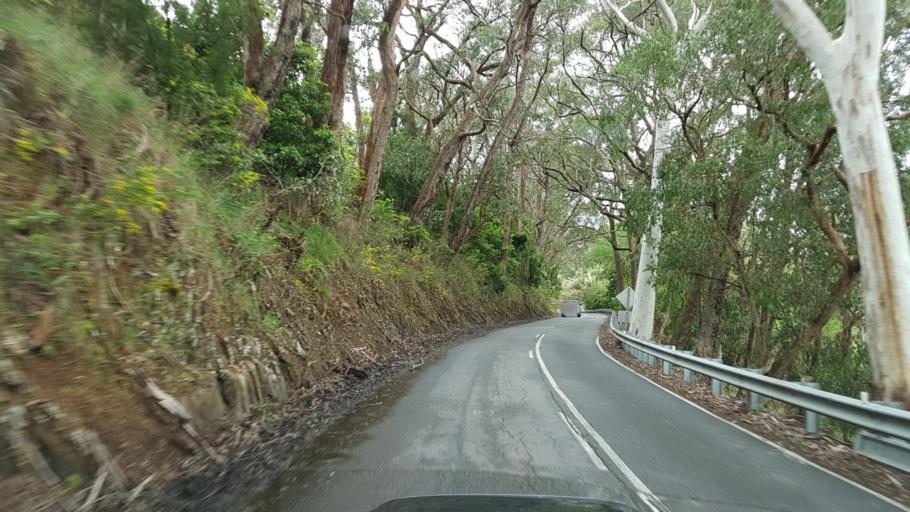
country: AU
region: South Australia
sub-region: Adelaide Hills
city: Lobethal
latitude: -34.9217
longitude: 138.8209
